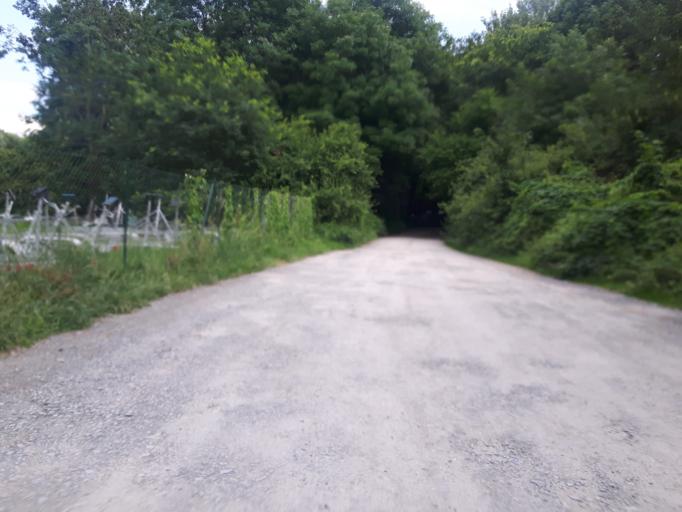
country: DE
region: Rheinland-Pfalz
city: Otterstadt
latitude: 49.3722
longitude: 8.4626
